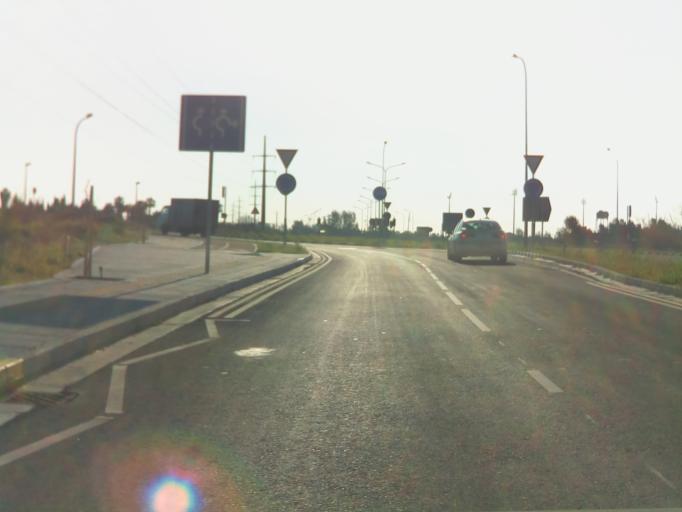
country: CY
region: Pafos
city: Paphos
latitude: 34.7492
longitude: 32.4335
